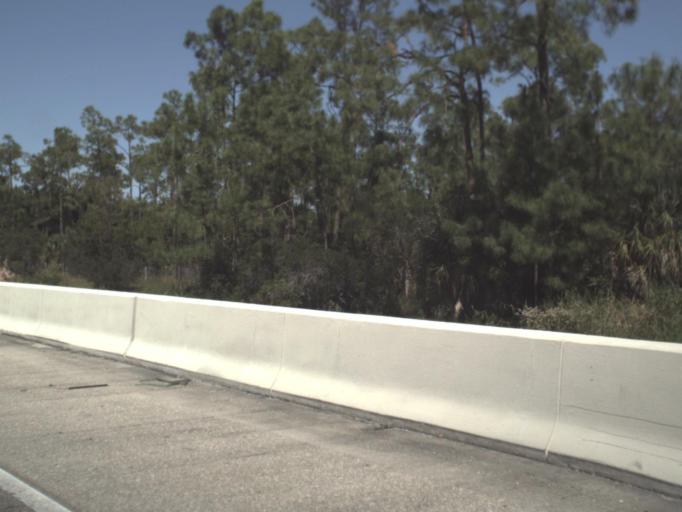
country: US
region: Florida
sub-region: Lee County
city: Three Oaks
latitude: 26.4495
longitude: -81.7839
